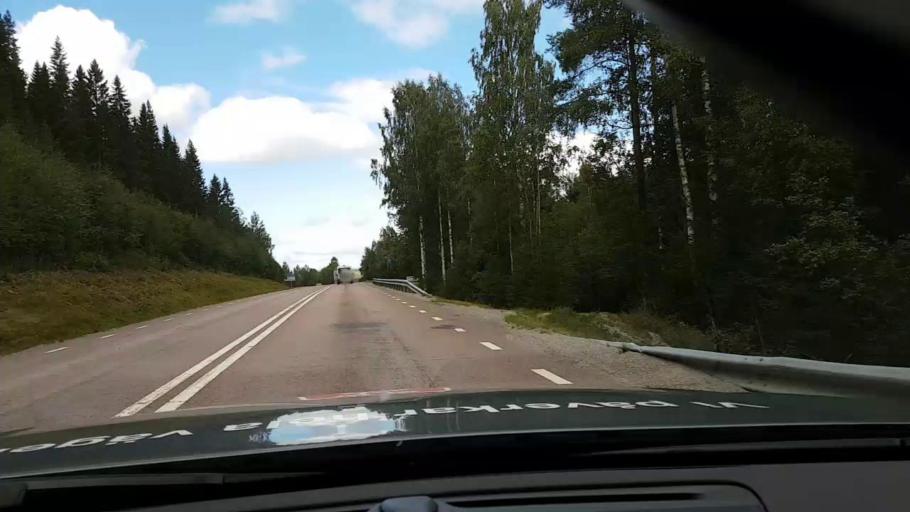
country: SE
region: Vaesternorrland
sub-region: OErnskoeldsviks Kommun
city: Bjasta
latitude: 63.3608
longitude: 18.4644
